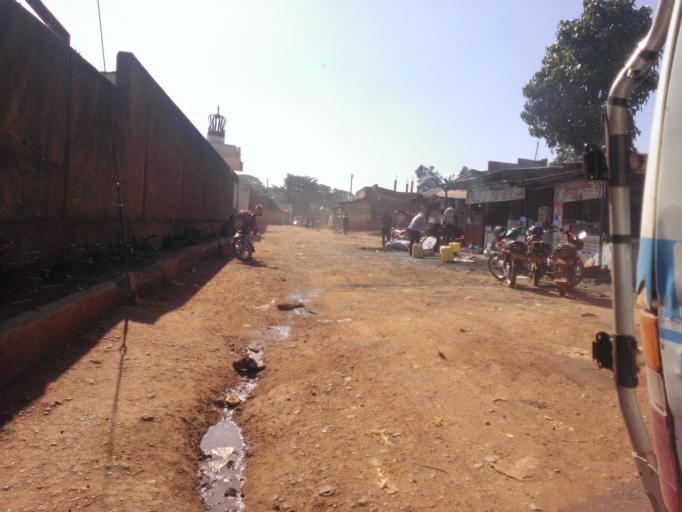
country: UG
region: Central Region
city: Kampala Central Division
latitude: 0.3282
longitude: 32.5603
